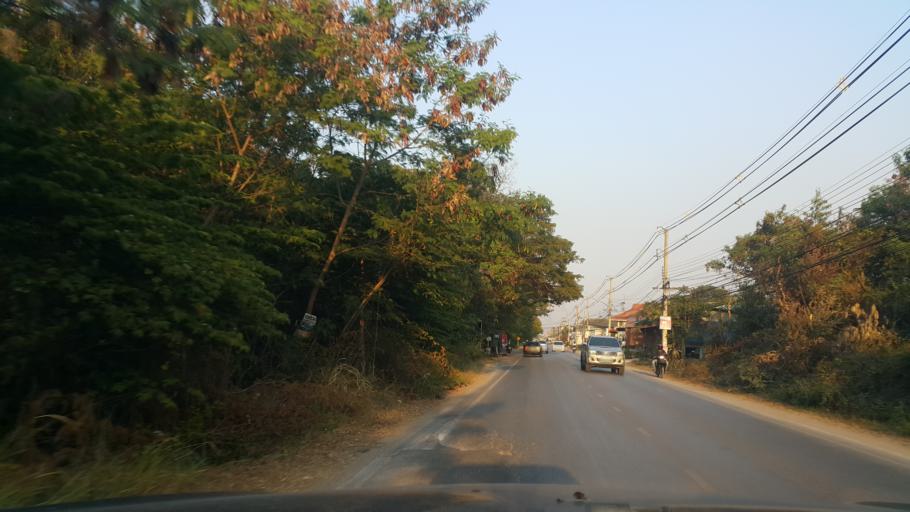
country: TH
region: Nakhon Ratchasima
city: Nakhon Ratchasima
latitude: 14.9381
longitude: 102.0309
